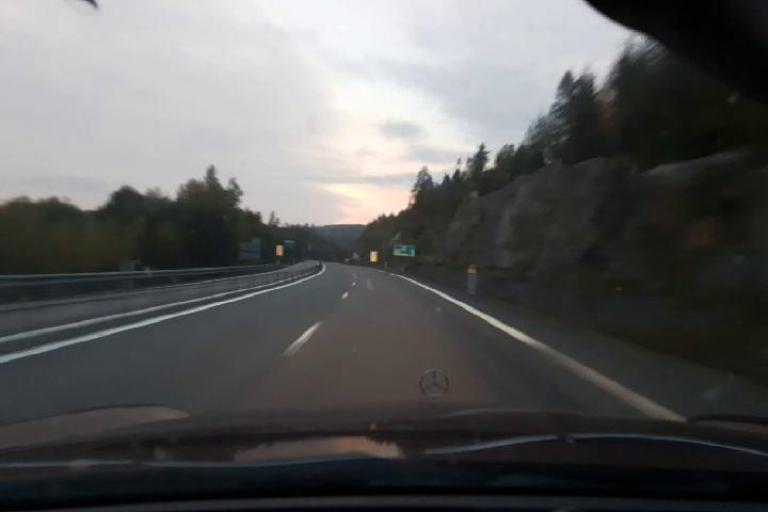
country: SE
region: Vaesternorrland
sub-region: Kramfors Kommun
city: Nordingra
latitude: 62.9466
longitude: 18.0932
